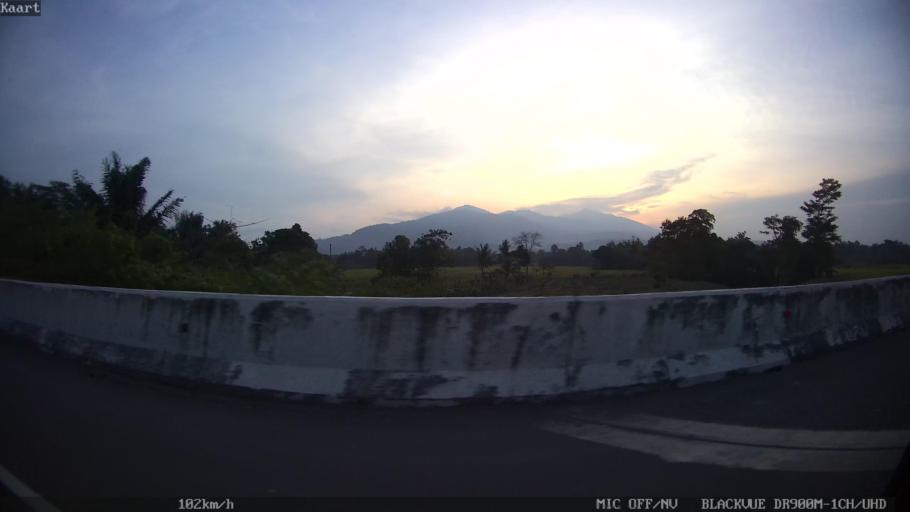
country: ID
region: Lampung
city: Penengahan
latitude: -5.7728
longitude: 105.7170
